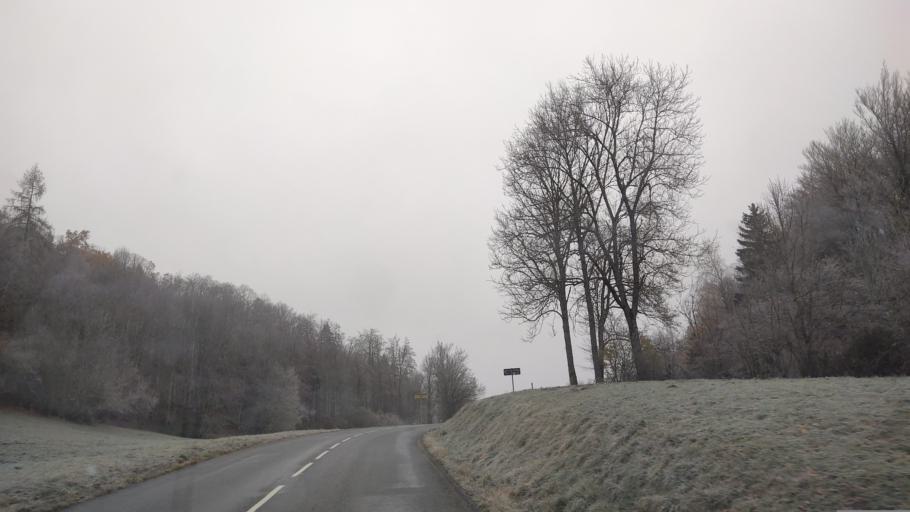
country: FR
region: Rhone-Alpes
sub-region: Departement de la Savoie
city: Coise-Saint-Jean-Pied-Gauthier
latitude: 45.5818
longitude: 6.1354
